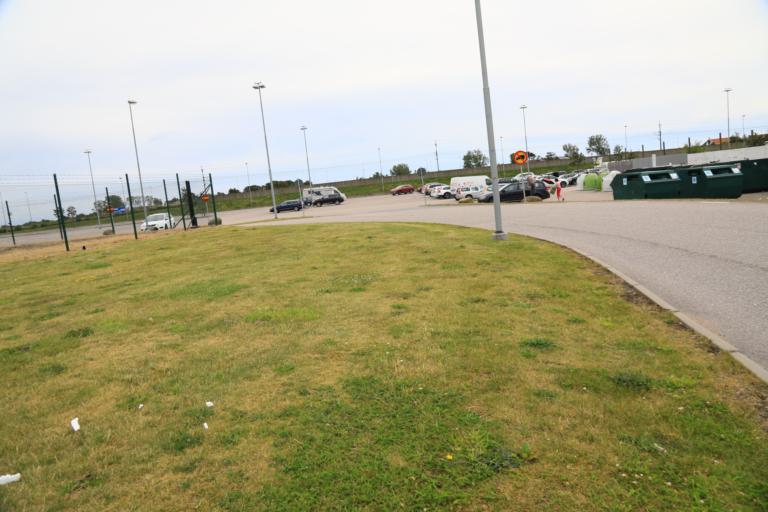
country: SE
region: Halland
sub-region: Varbergs Kommun
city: Traslovslage
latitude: 57.0826
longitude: 12.2803
